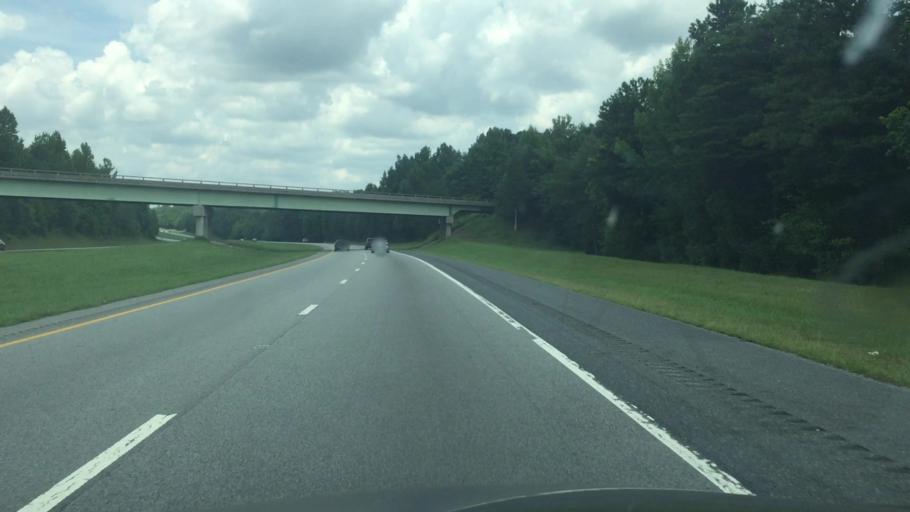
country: US
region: North Carolina
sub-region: Guilford County
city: Pleasant Garden
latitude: 35.9520
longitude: -79.8208
